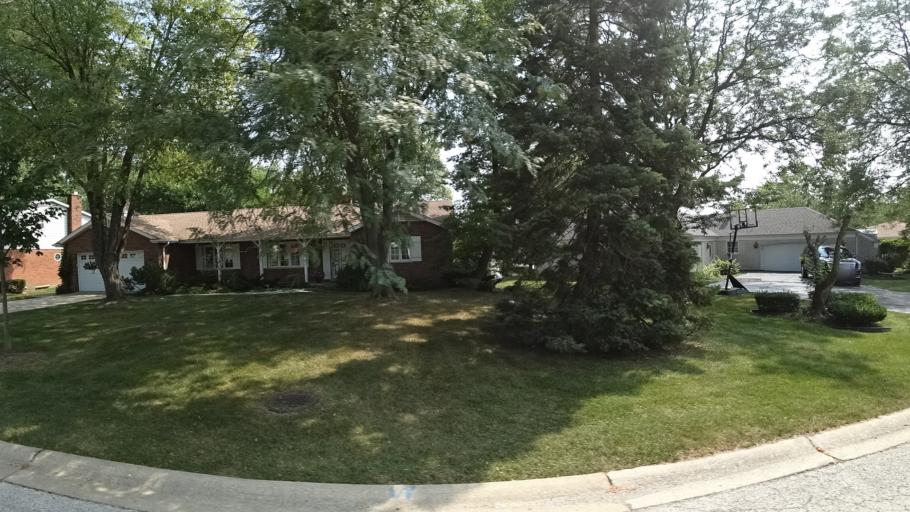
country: US
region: Illinois
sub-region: Cook County
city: Orland Park
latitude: 41.6245
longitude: -87.8723
